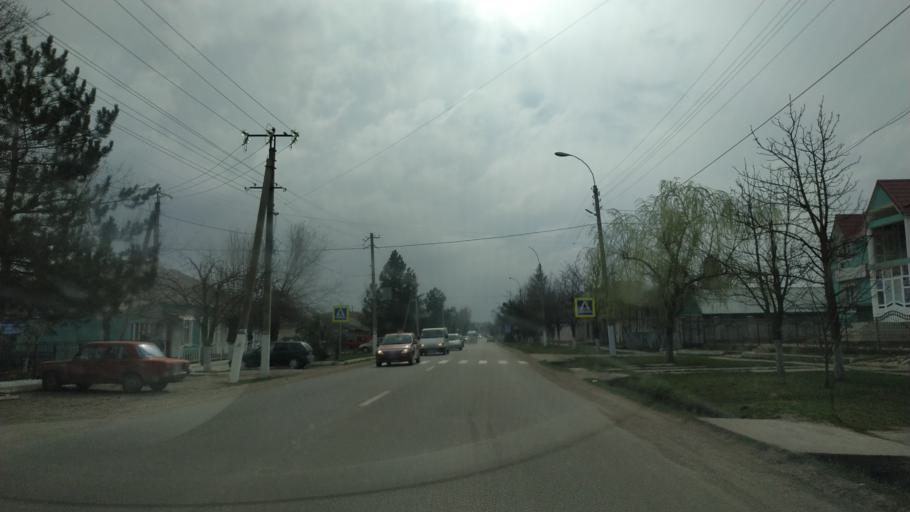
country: MD
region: Basarabeasca
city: Basarabeasca
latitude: 46.3372
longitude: 28.9579
